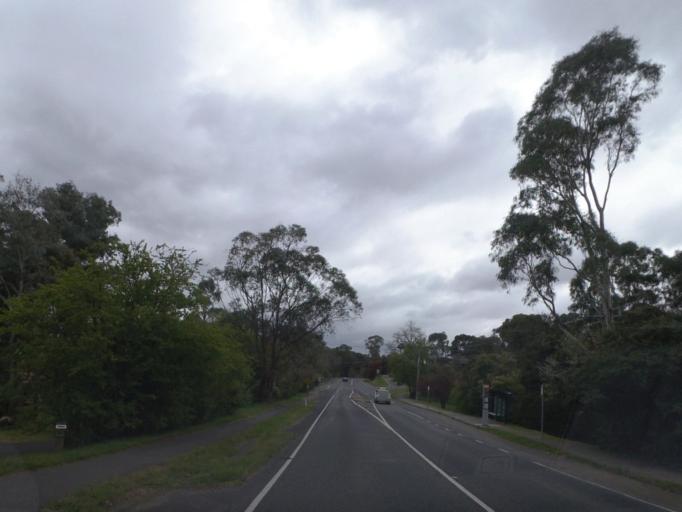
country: AU
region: Victoria
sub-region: Nillumbik
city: North Warrandyte
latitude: -37.7444
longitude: 145.2107
